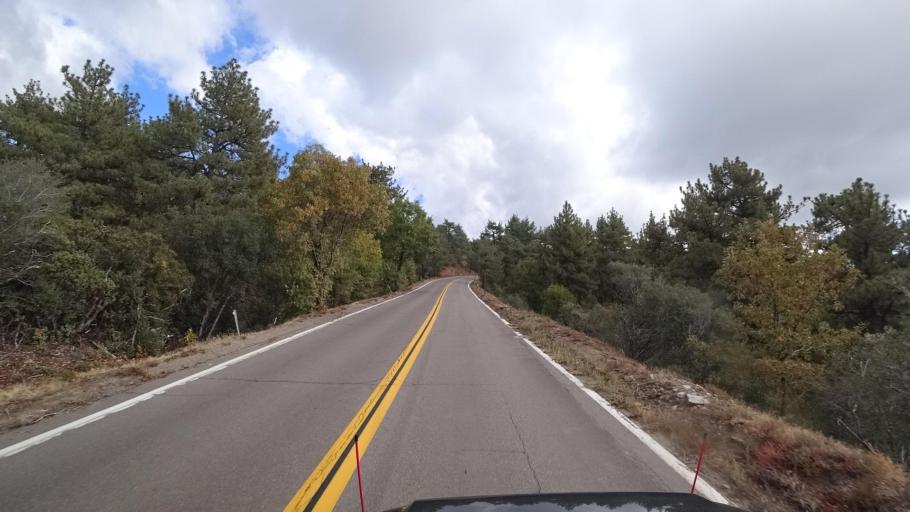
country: US
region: California
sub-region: San Diego County
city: Pine Valley
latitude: 32.8574
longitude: -116.4569
